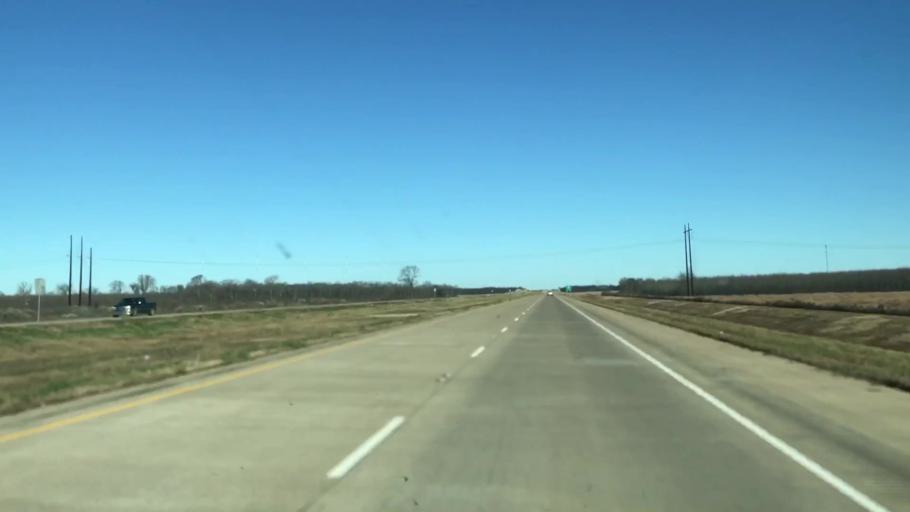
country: US
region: Louisiana
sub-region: Caddo Parish
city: Blanchard
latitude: 32.6639
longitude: -93.8455
